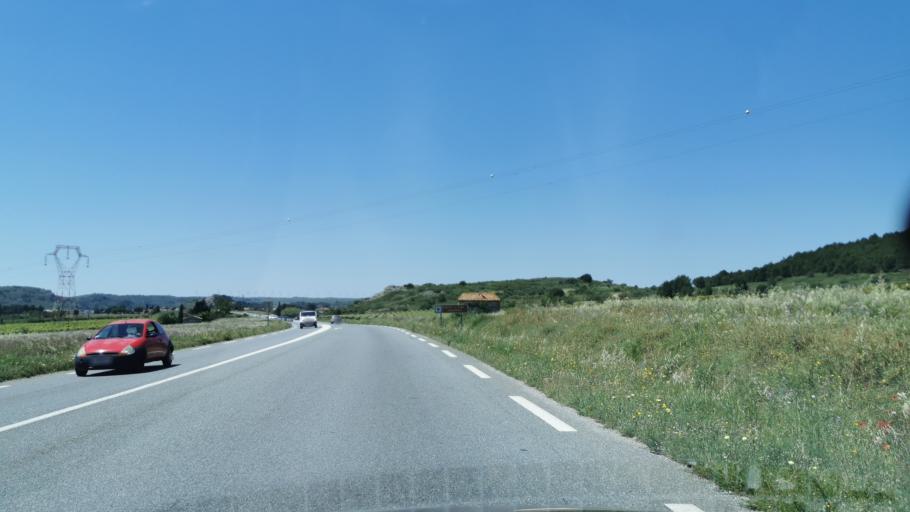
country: FR
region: Languedoc-Roussillon
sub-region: Departement de l'Aude
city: Narbonne
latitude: 43.1820
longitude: 2.9530
